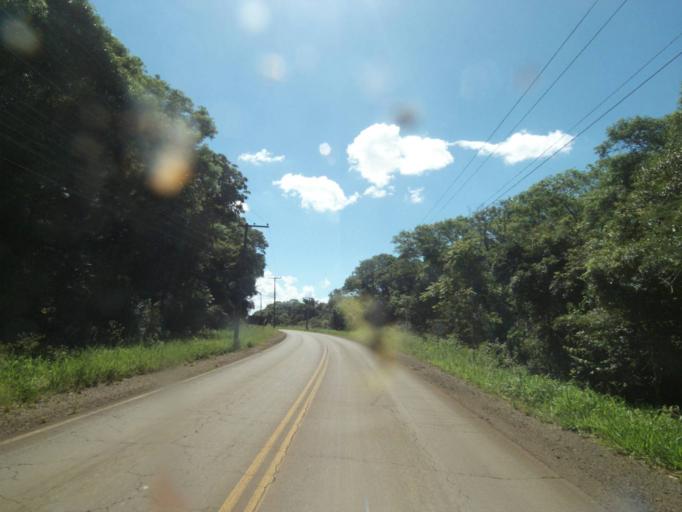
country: BR
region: Parana
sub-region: Chopinzinho
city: Chopinzinho
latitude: -25.7866
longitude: -52.0964
